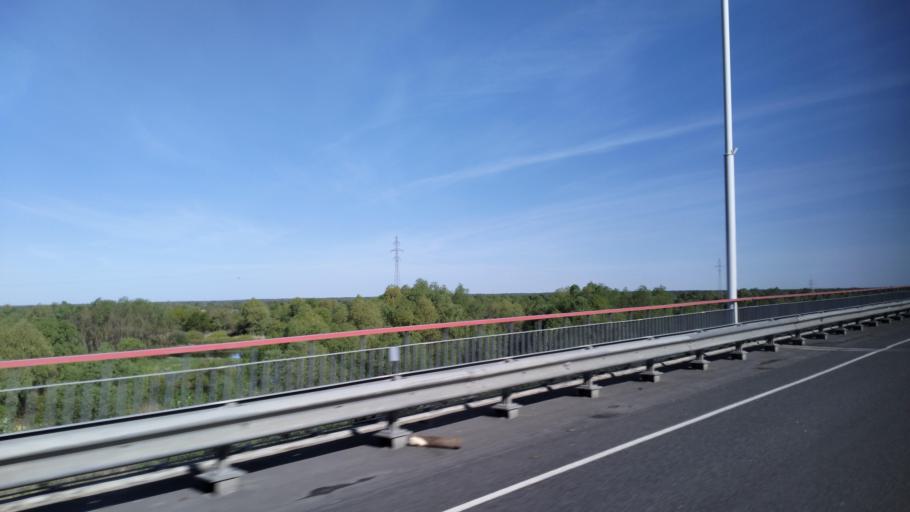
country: BY
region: Gomel
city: Turaw
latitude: 52.0761
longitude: 27.8254
